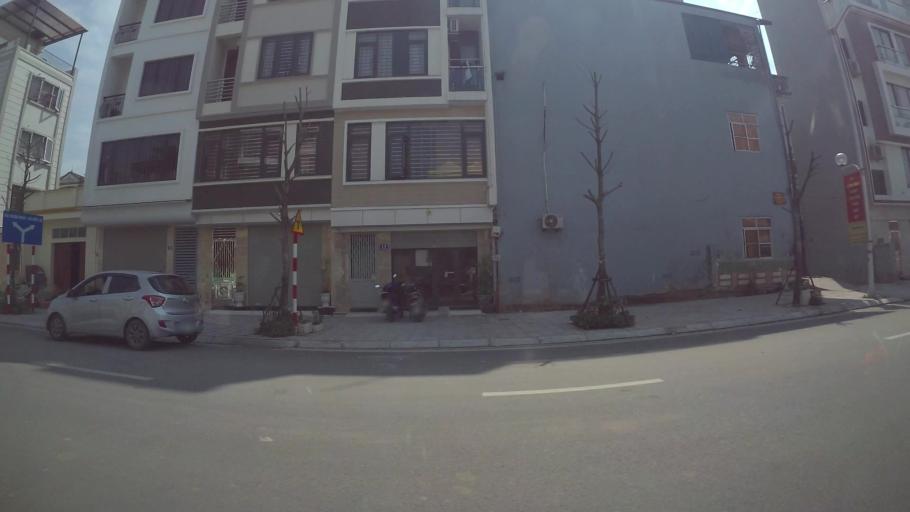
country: VN
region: Ha Noi
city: Hoan Kiem
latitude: 21.0633
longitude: 105.8675
